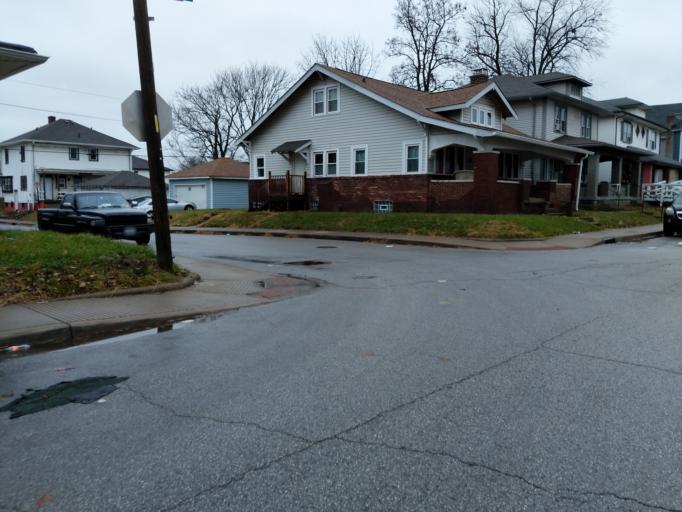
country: US
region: Indiana
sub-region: Marion County
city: Indianapolis
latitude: 39.7688
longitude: -86.1264
